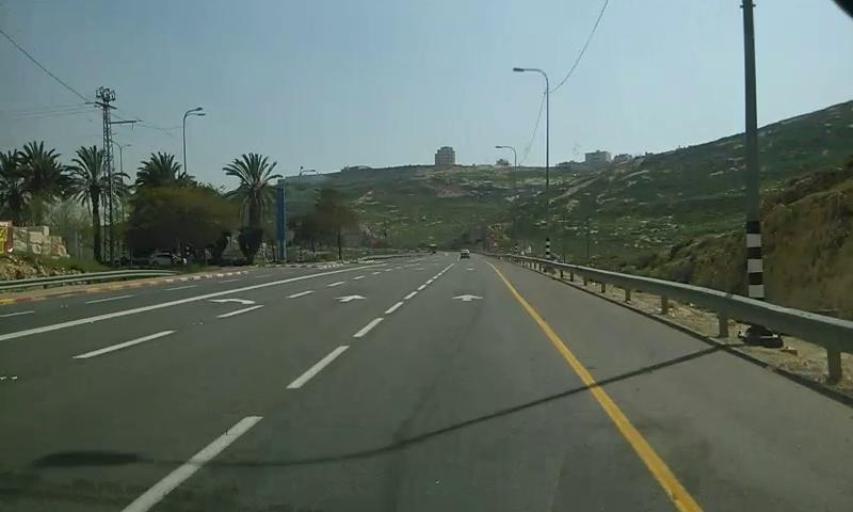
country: PS
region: West Bank
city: Jaba`
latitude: 31.8645
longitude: 35.2594
